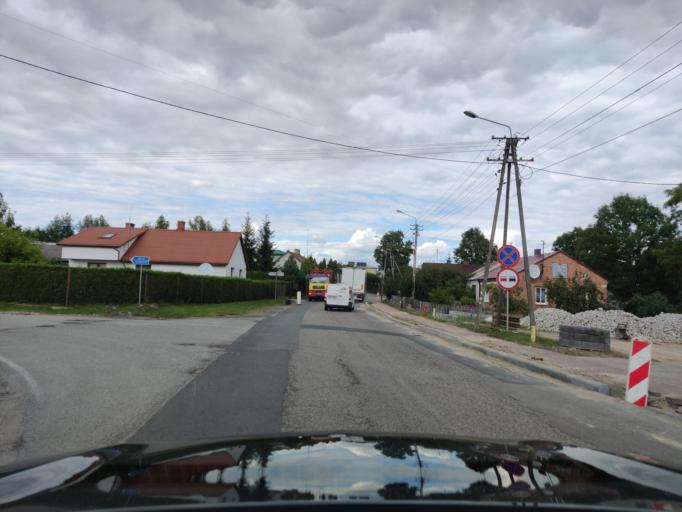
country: PL
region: Masovian Voivodeship
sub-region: Powiat sokolowski
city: Ceranow
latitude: 52.6337
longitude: 22.2302
